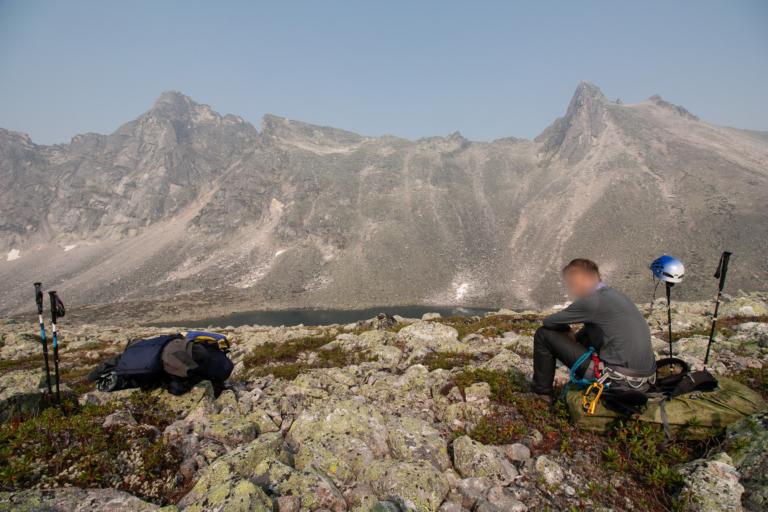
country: RU
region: Respublika Buryatiya
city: Kichera
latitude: 56.2396
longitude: 110.6903
